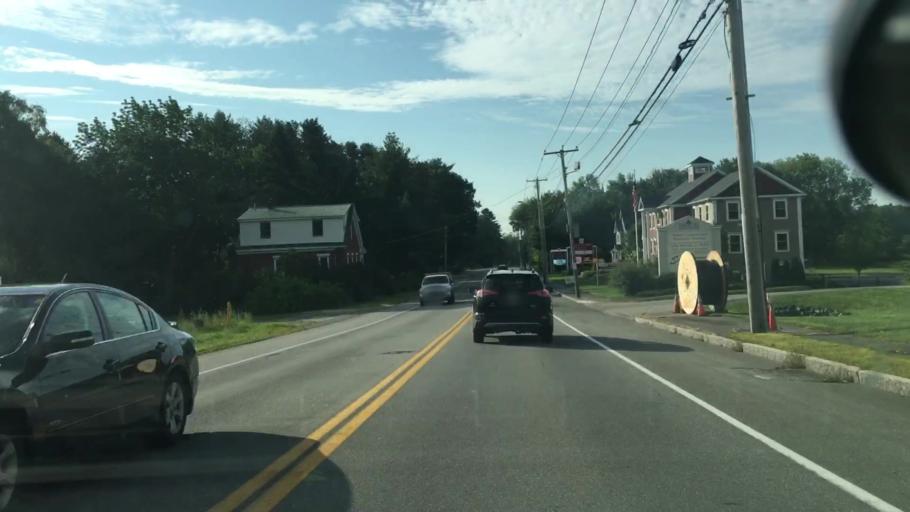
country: US
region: Maine
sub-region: Cumberland County
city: Westbrook
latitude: 43.7105
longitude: -70.3305
